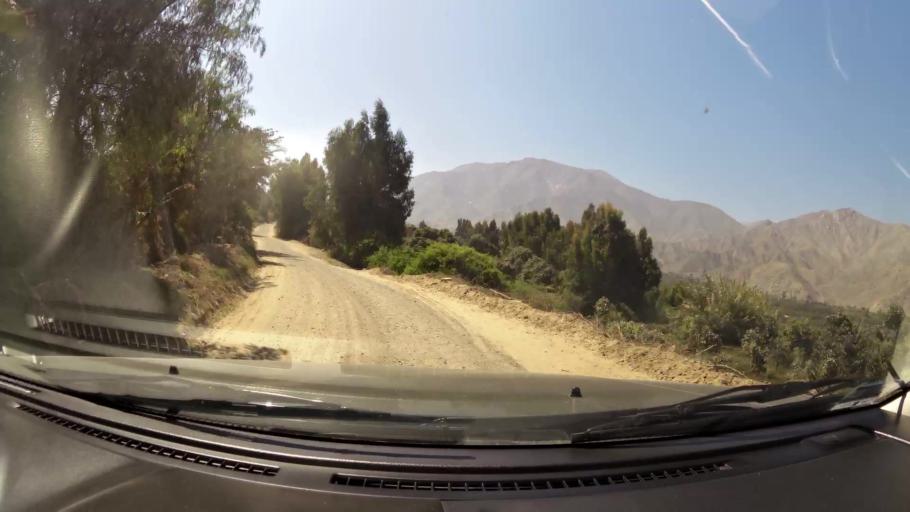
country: PE
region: Ica
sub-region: Provincia de Ica
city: Guadalupe
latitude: -13.8784
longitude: -75.6452
